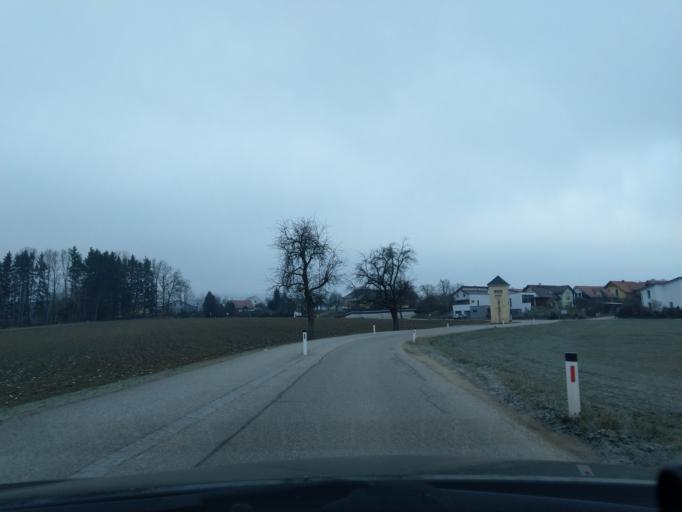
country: AT
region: Upper Austria
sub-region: Politischer Bezirk Urfahr-Umgebung
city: Engerwitzdorf
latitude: 48.3707
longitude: 14.5217
